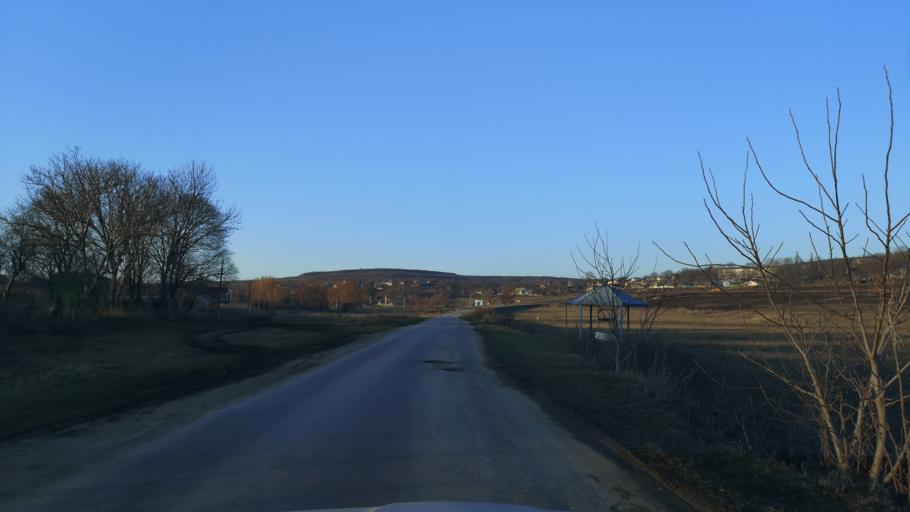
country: MD
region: Orhei
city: Orhei
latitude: 47.3498
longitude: 28.6961
